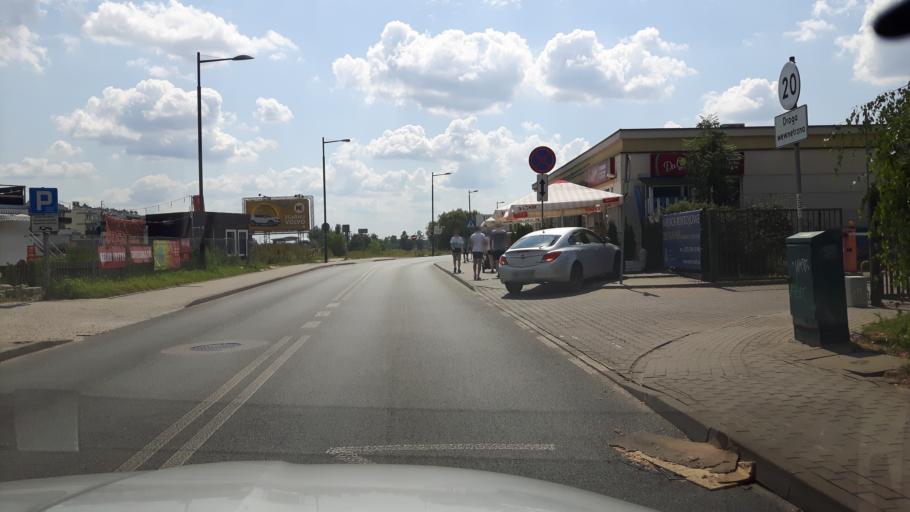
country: PL
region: Masovian Voivodeship
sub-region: Warszawa
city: Targowek
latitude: 52.3158
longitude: 21.0600
